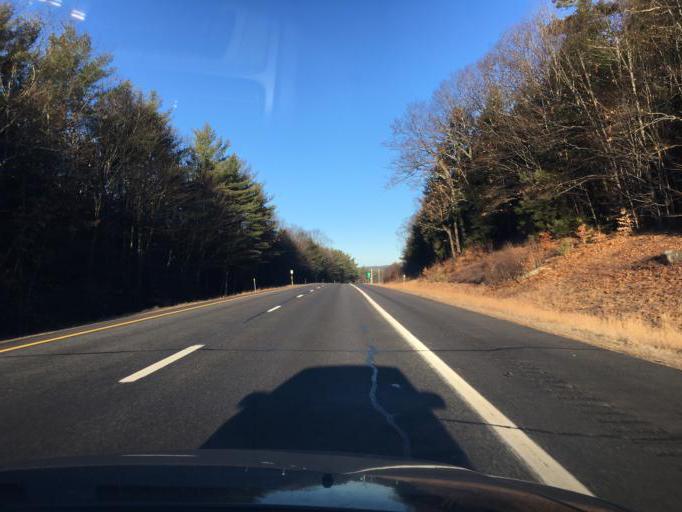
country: US
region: New Hampshire
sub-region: Belknap County
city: Sanbornton
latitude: 43.4997
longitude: -71.6095
